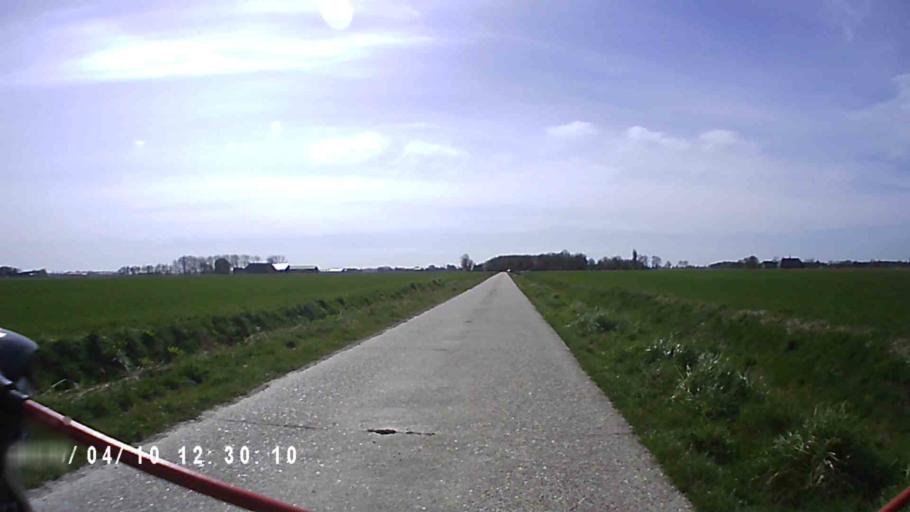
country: NL
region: Groningen
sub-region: Gemeente De Marne
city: Ulrum
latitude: 53.4012
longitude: 6.4100
